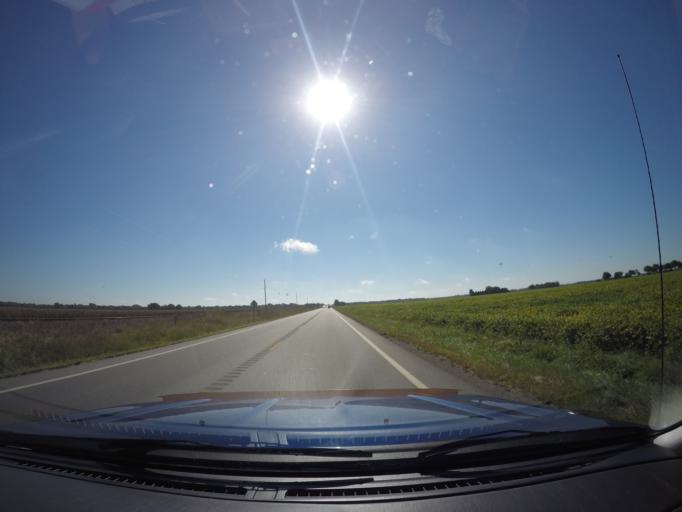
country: US
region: Kansas
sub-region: Shawnee County
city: Rossville
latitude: 39.1500
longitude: -95.9786
